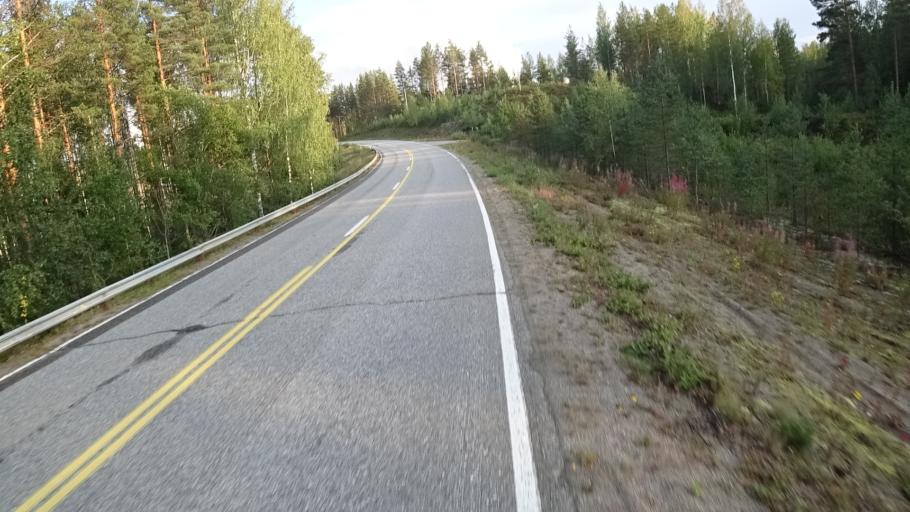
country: FI
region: North Karelia
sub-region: Joensuu
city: Ilomantsi
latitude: 62.6299
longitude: 31.0939
